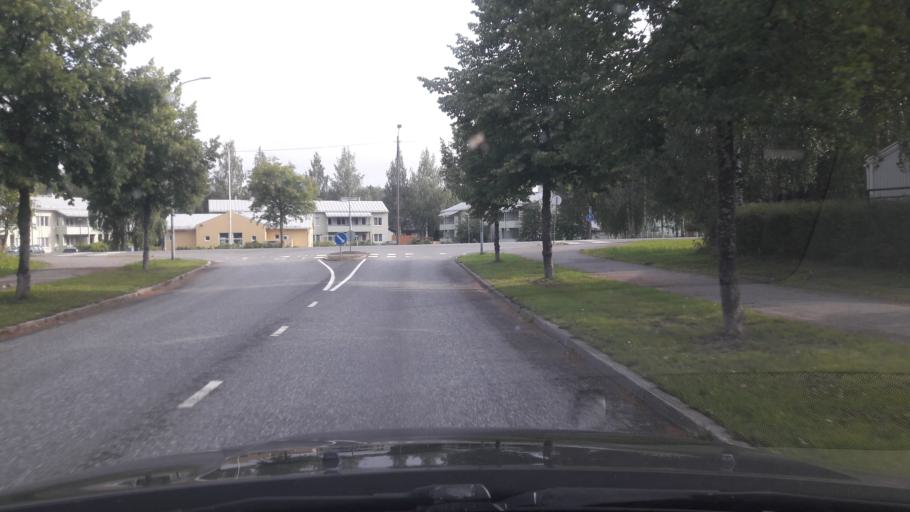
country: FI
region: North Karelia
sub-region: Joensuu
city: Joensuu
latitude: 62.5995
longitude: 29.8280
